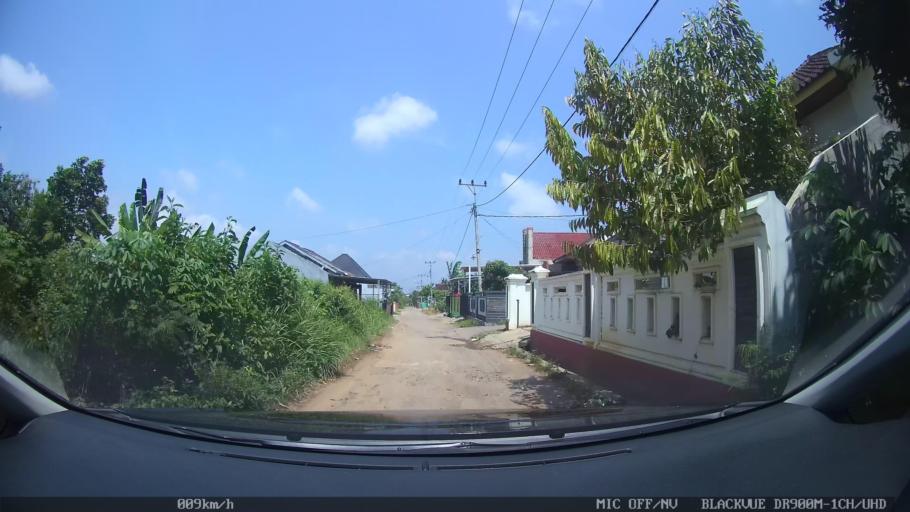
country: ID
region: Lampung
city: Kedaton
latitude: -5.3540
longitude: 105.2781
